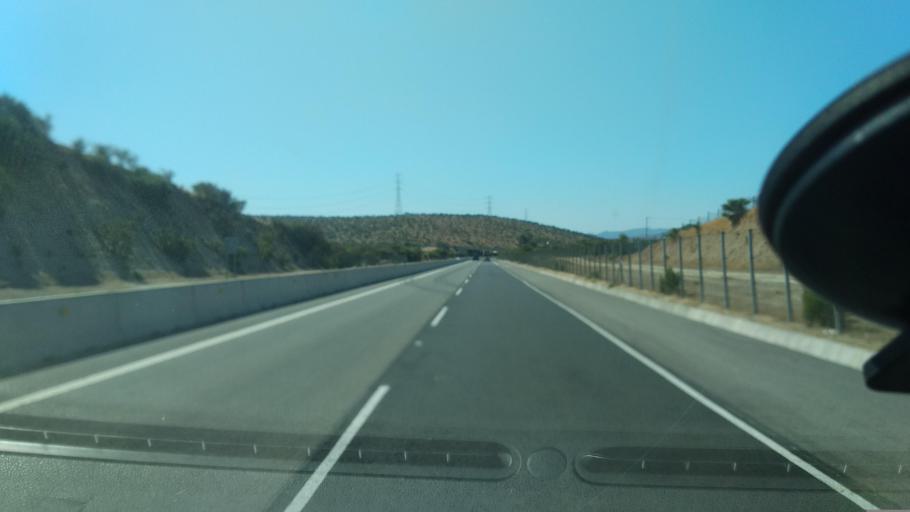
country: CL
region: Valparaiso
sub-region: Provincia de Marga Marga
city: Villa Alemana
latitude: -33.0102
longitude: -71.3249
